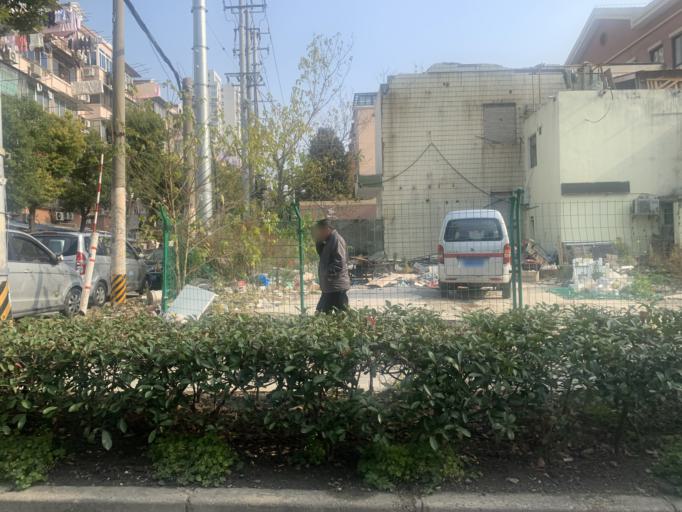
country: CN
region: Shanghai Shi
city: Huamu
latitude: 31.1846
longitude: 121.5150
